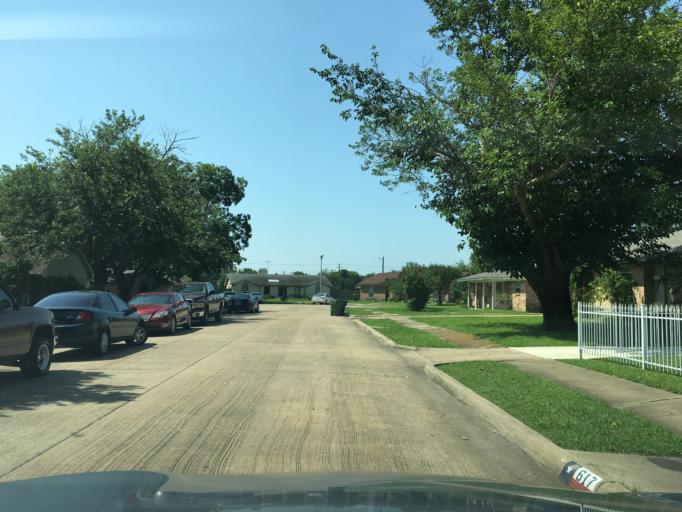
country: US
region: Texas
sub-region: Dallas County
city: Richardson
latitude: 32.9189
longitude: -96.6917
